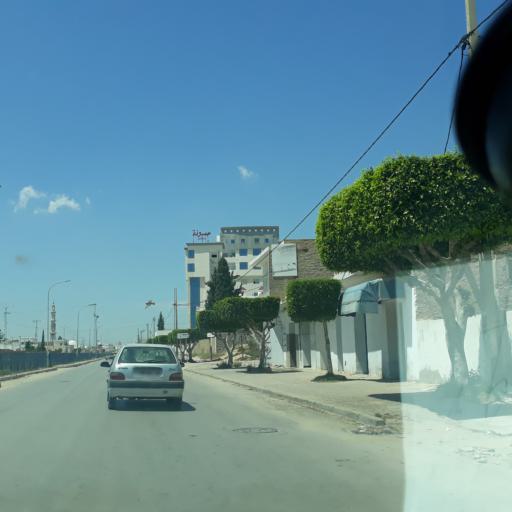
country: TN
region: Safaqis
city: Al Qarmadah
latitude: 34.8050
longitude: 10.7576
